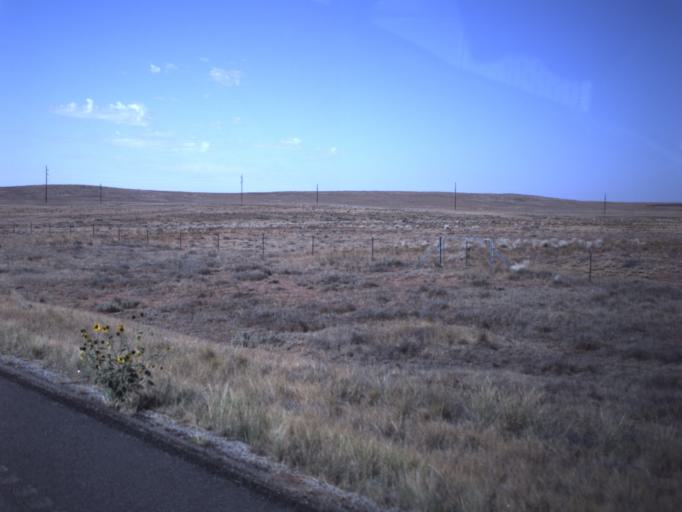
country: US
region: Utah
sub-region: San Juan County
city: Blanding
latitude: 37.4040
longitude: -109.4916
